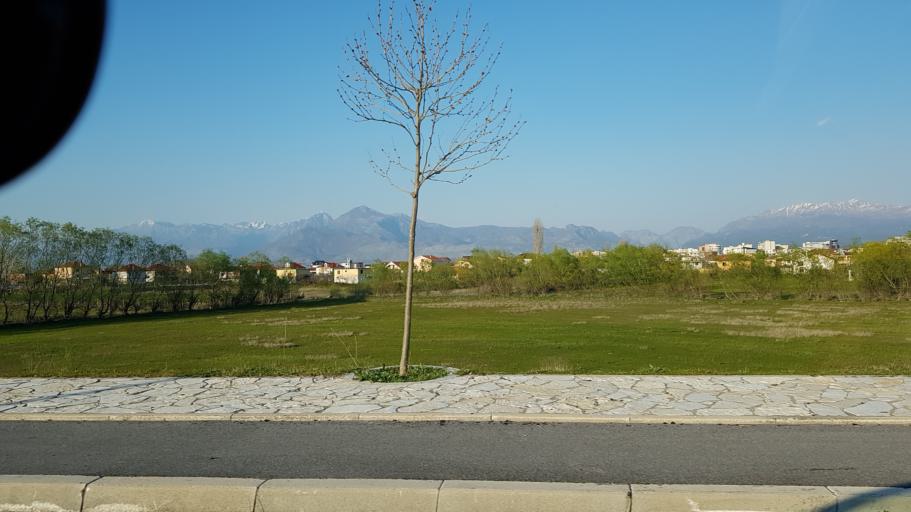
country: AL
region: Shkoder
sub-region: Rrethi i Shkodres
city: Shkoder
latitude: 42.0625
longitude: 19.4937
